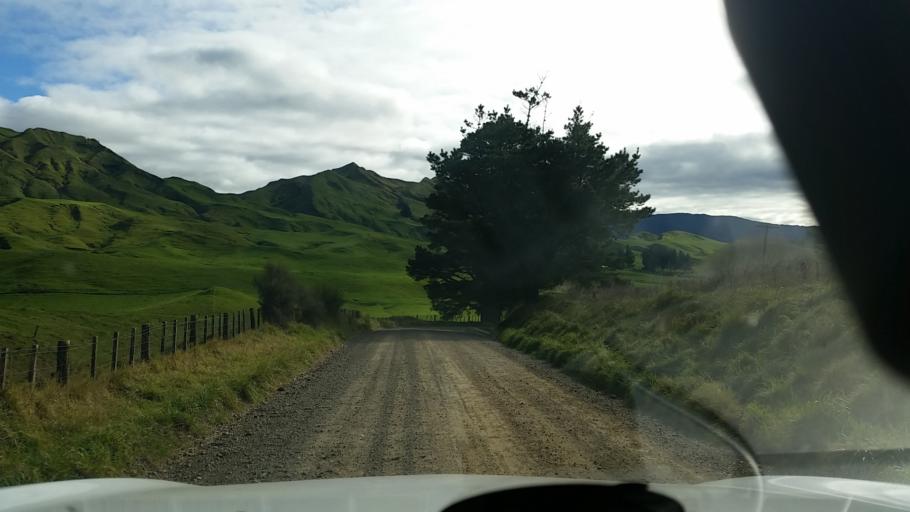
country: NZ
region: Hawke's Bay
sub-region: Napier City
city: Napier
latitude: -39.1296
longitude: 176.8957
